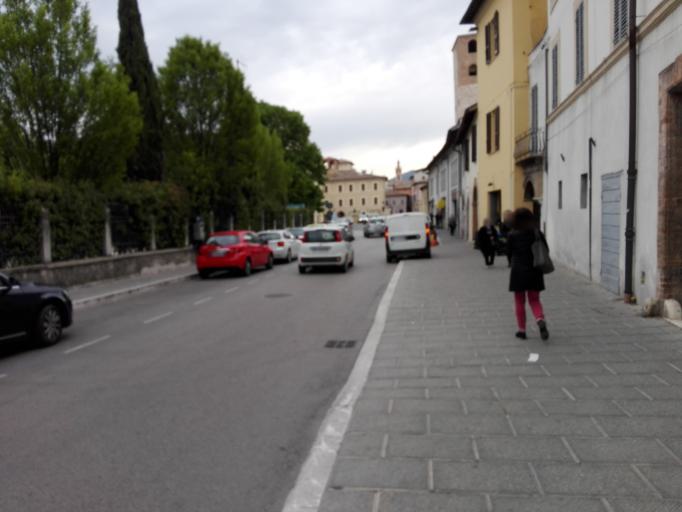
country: IT
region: Umbria
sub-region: Provincia di Perugia
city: Foligno
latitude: 42.9530
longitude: 12.6992
